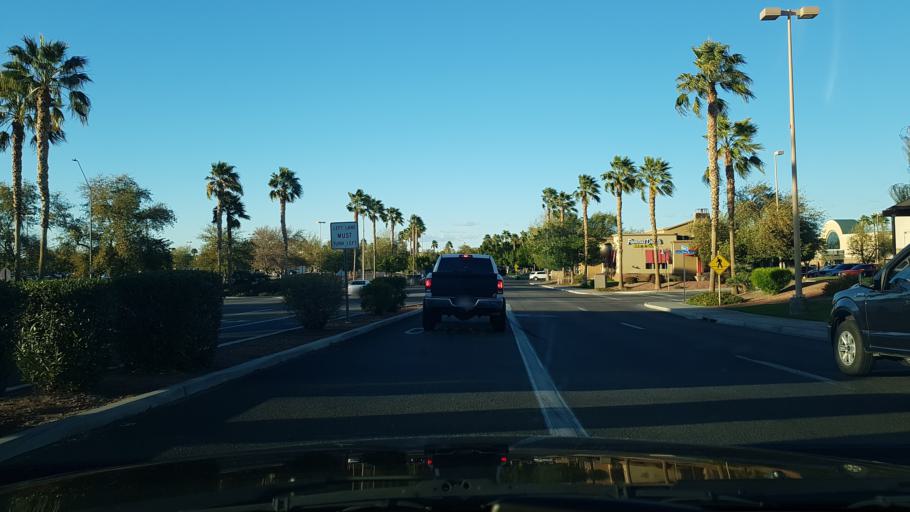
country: US
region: Arizona
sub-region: Yuma County
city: Yuma
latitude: 32.6994
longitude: -114.6030
